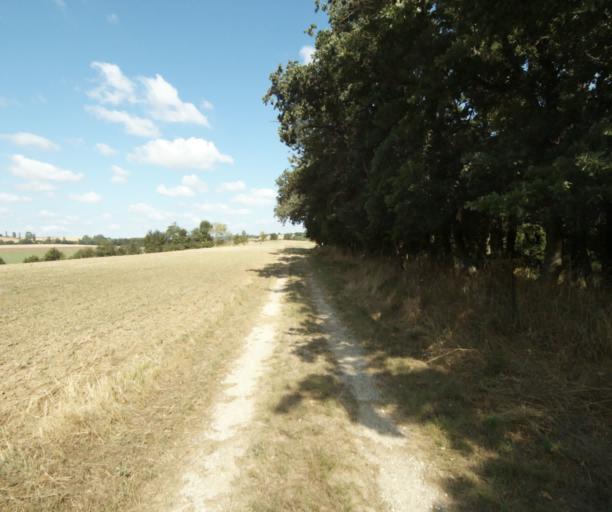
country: FR
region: Midi-Pyrenees
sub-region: Departement de la Haute-Garonne
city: Avignonet-Lauragais
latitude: 43.4439
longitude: 1.7881
